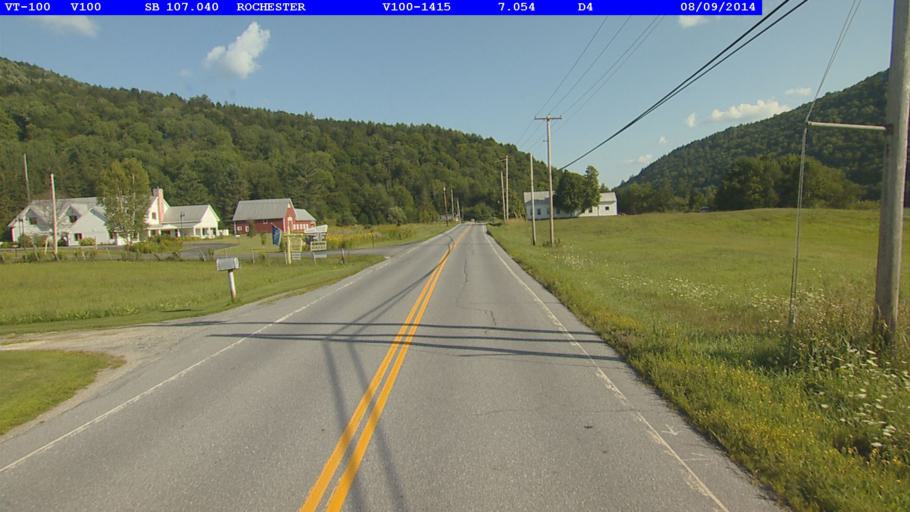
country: US
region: Vermont
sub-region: Orange County
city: Randolph
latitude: 43.8964
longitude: -72.8200
